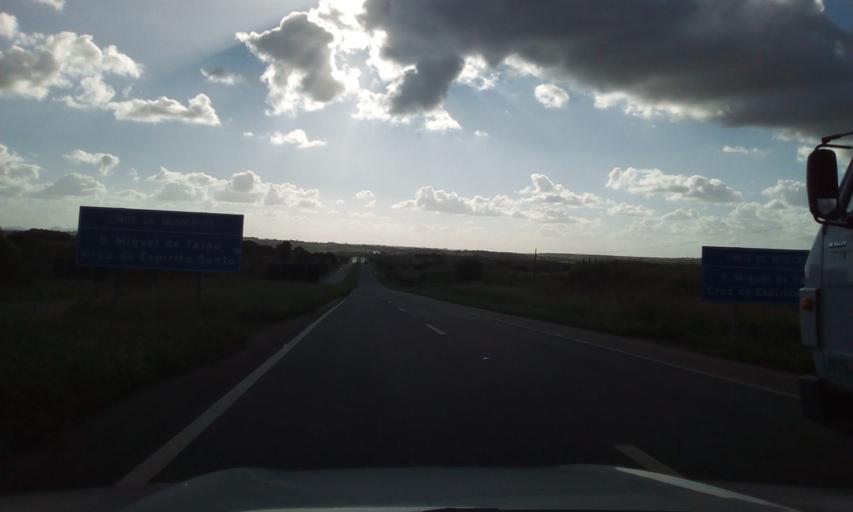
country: BR
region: Paraiba
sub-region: Cruz Do Espirito Santo
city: Cruz do Espirito Santo
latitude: -7.1982
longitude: -35.1663
